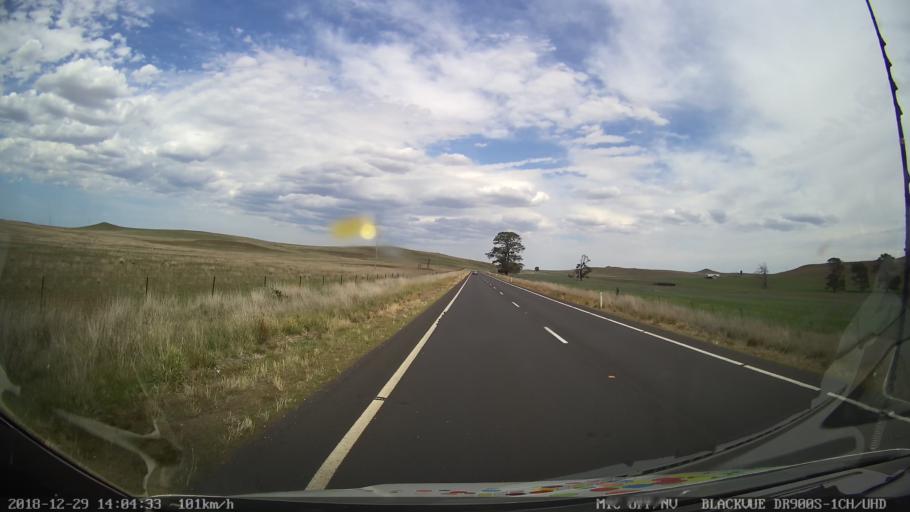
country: AU
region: New South Wales
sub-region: Cooma-Monaro
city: Cooma
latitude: -36.3177
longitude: 149.1872
